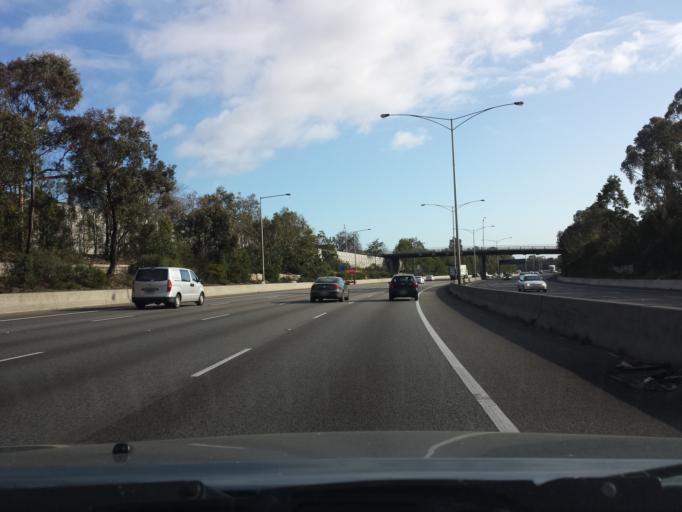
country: AU
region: Victoria
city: Carnegie
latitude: -37.8748
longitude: 145.0668
